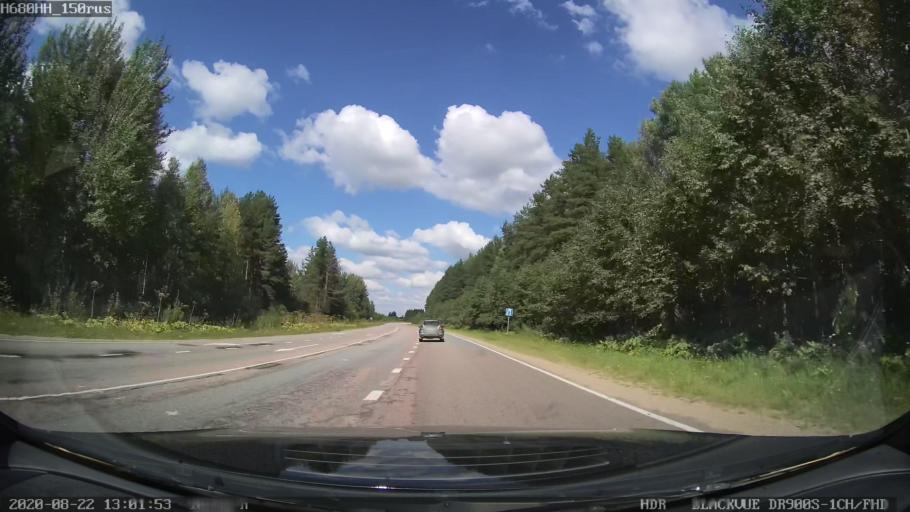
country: RU
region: Tverskaya
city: Bezhetsk
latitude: 57.6414
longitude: 36.3952
